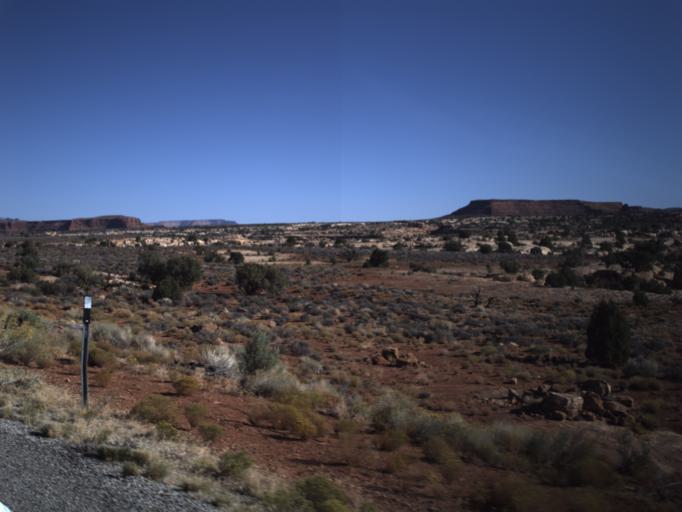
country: US
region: Utah
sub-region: San Juan County
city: Blanding
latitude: 37.7716
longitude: -110.2876
